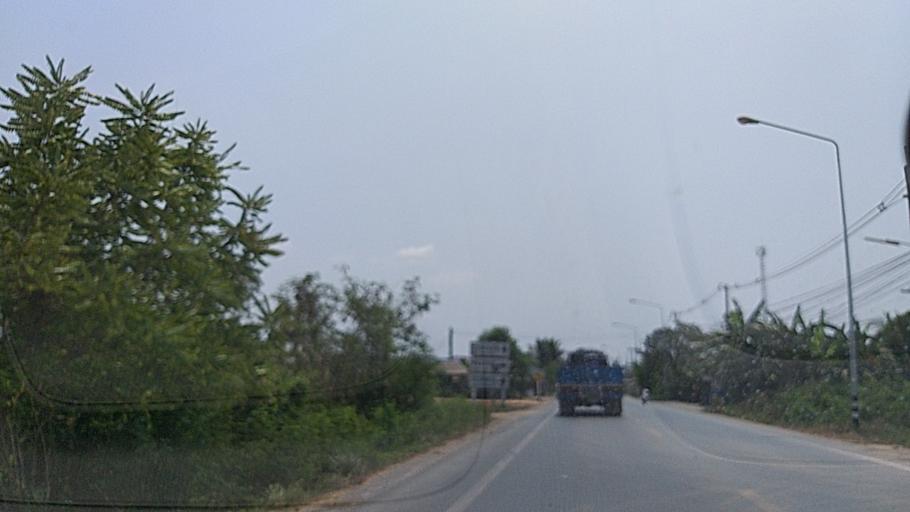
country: TH
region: Chachoengsao
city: Bang Nam Priao
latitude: 13.9433
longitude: 100.9780
